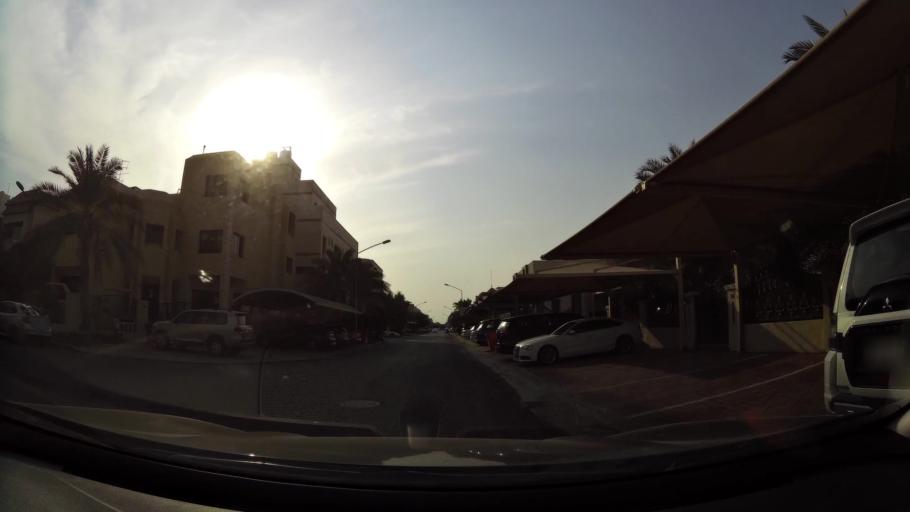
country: KW
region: Muhafazat Hawalli
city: Hawalli
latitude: 29.3084
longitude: 48.0123
